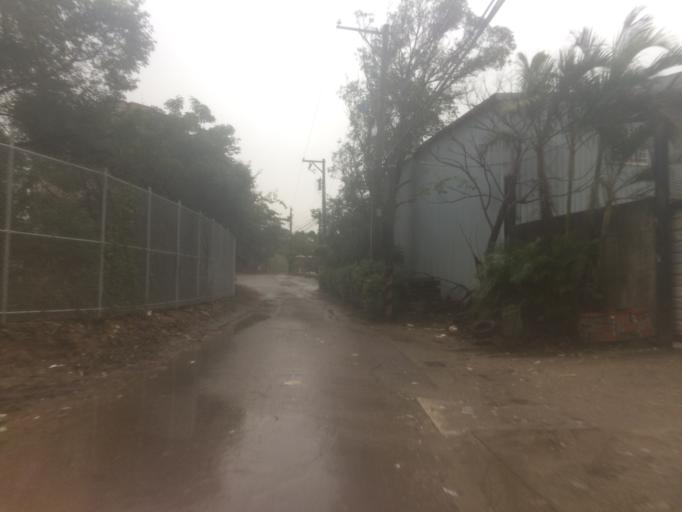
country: TW
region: Taiwan
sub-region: Hsinchu
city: Hsinchu
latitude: 24.7643
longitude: 120.9673
